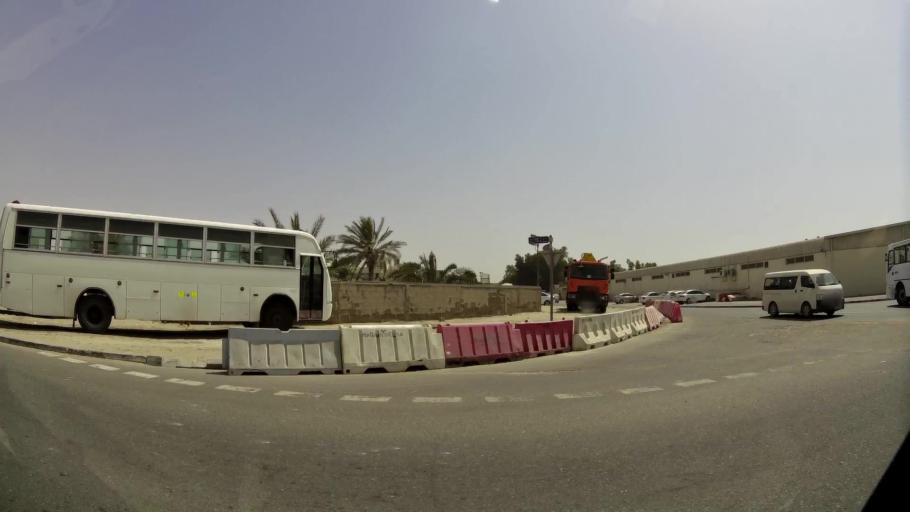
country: AE
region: Dubai
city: Dubai
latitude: 25.1375
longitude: 55.2357
